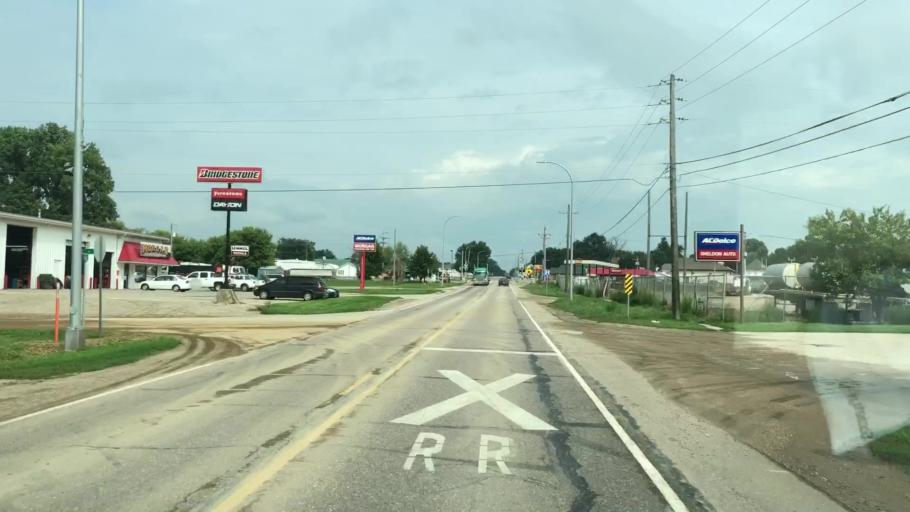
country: US
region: Iowa
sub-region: O'Brien County
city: Sheldon
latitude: 43.1858
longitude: -95.8576
